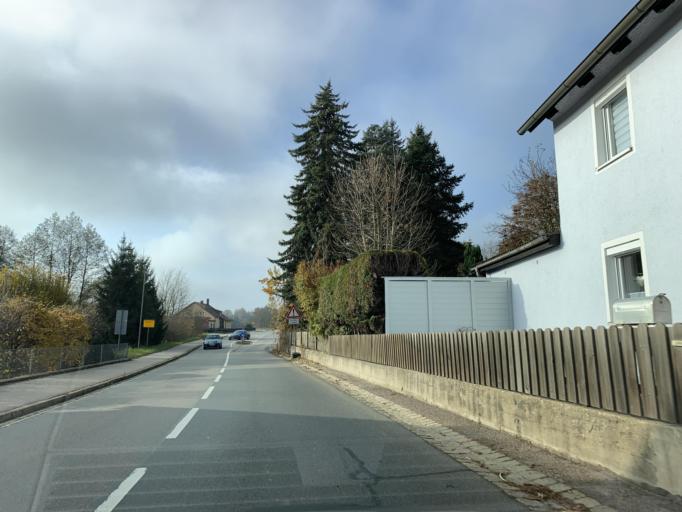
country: DE
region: Bavaria
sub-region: Upper Palatinate
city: Bodenwohr
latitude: 49.2673
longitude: 12.2997
